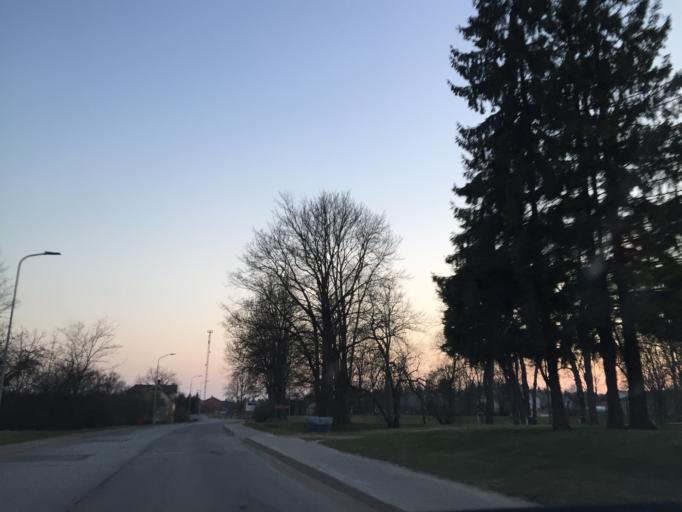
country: LV
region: Valkas Rajons
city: Valka
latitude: 57.7678
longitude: 26.0088
